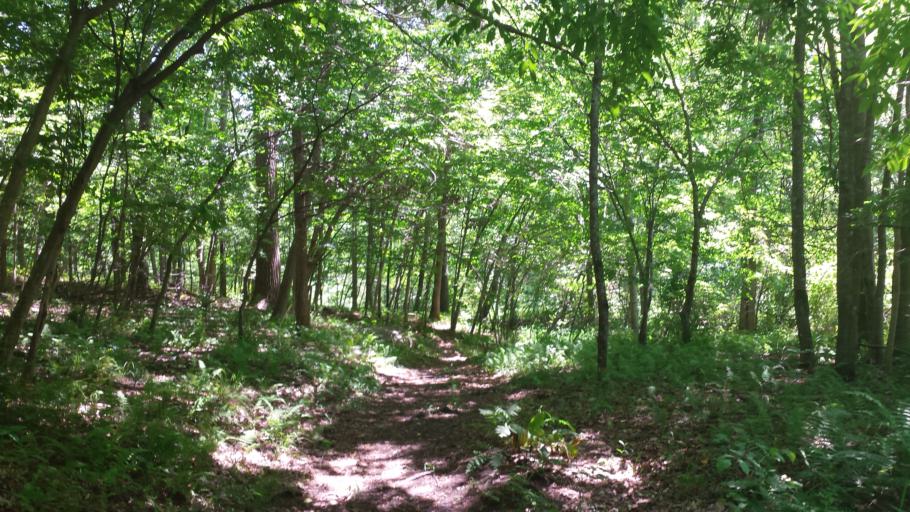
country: US
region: New York
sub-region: Westchester County
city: Pound Ridge
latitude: 41.2579
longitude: -73.5742
